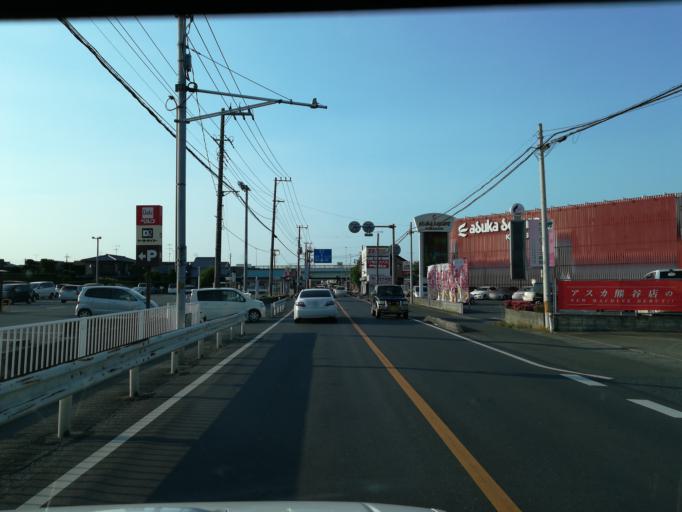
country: JP
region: Saitama
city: Kumagaya
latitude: 36.1642
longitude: 139.3847
